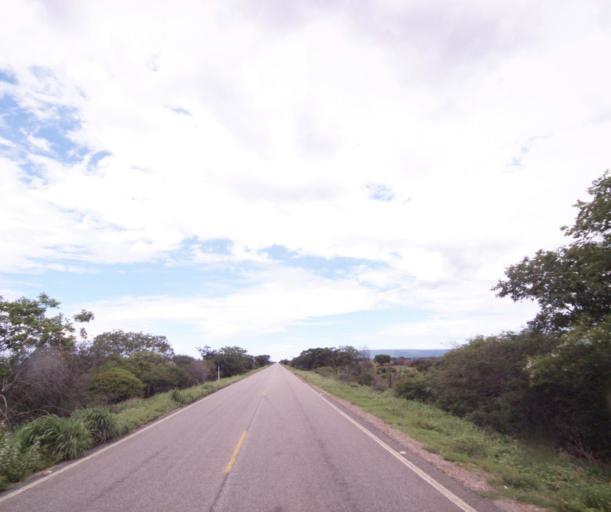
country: BR
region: Bahia
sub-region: Palmas De Monte Alto
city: Palmas de Monte Alto
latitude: -14.2578
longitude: -43.2641
